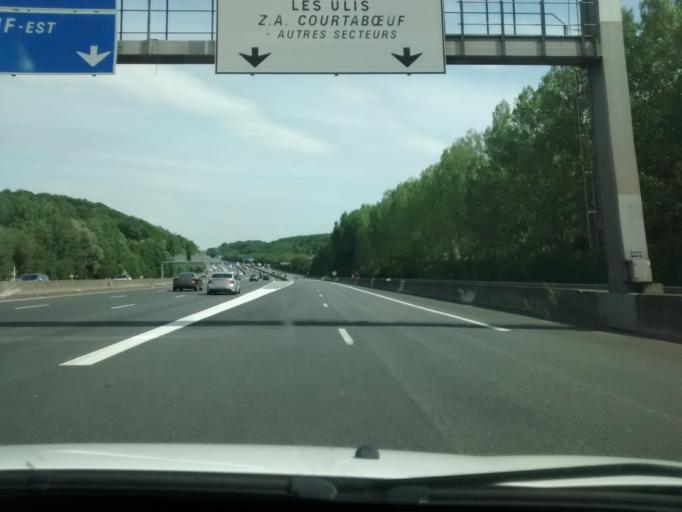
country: FR
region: Ile-de-France
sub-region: Departement de l'Essonne
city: Les Ulis
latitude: 48.6576
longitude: 2.1823
